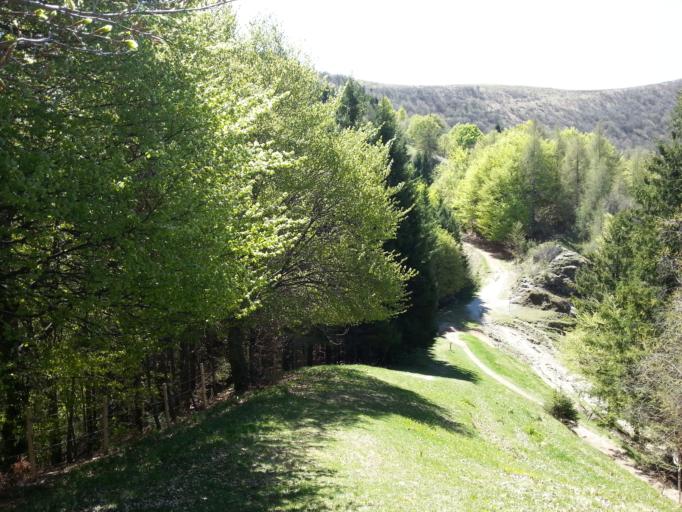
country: IT
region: Lombardy
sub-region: Provincia di Como
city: Magreglio
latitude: 45.9206
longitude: 9.2380
